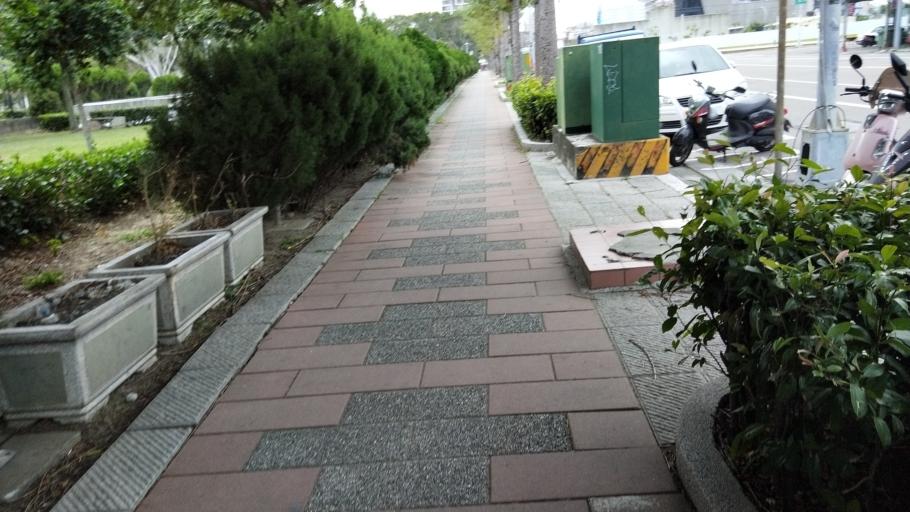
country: TW
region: Taiwan
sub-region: Hsinchu
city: Hsinchu
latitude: 24.6905
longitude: 120.8890
